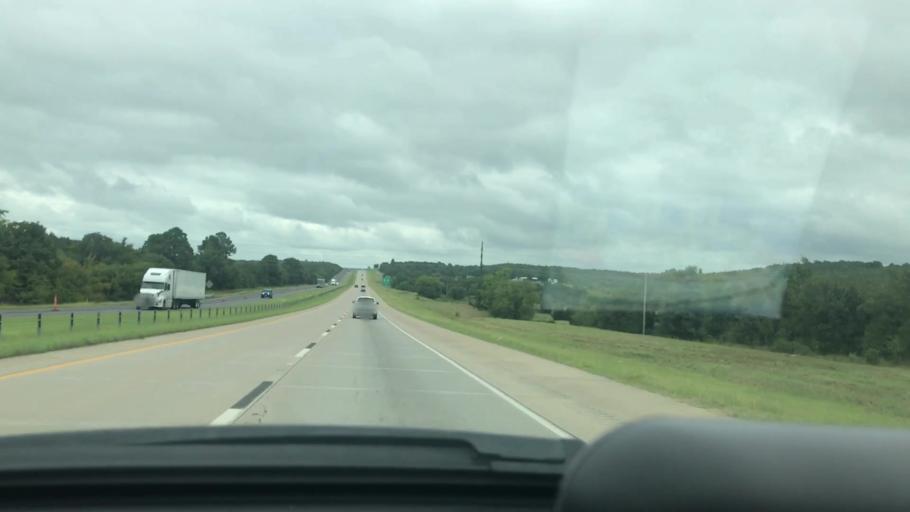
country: US
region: Oklahoma
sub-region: Pittsburg County
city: Krebs
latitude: 34.9749
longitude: -95.7233
